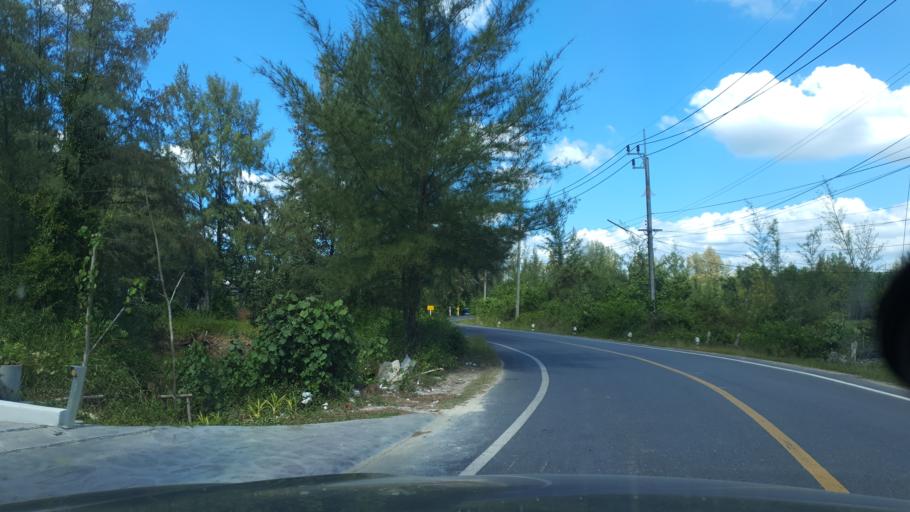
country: TH
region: Phangnga
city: Thai Mueang
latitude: 8.2843
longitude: 98.2753
